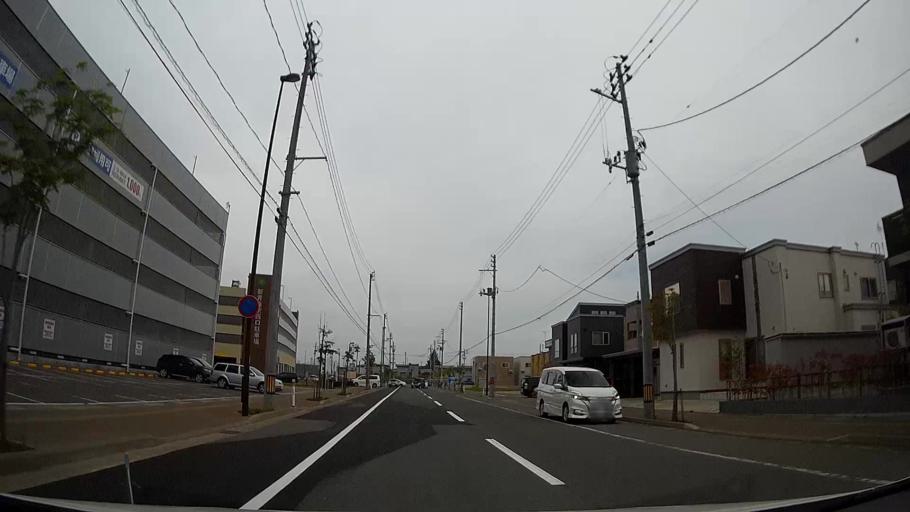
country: JP
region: Aomori
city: Aomori Shi
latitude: 40.8296
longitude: 140.6922
